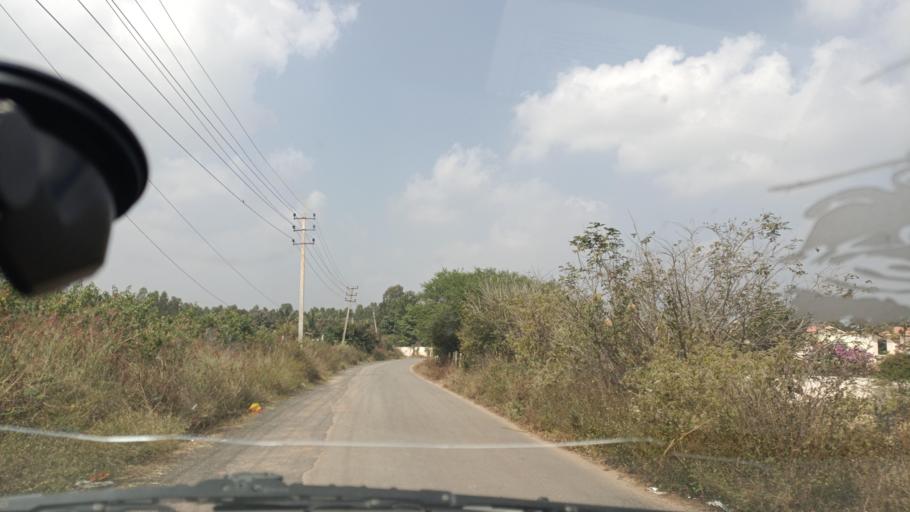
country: IN
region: Karnataka
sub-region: Bangalore Urban
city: Yelahanka
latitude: 13.1502
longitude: 77.6342
